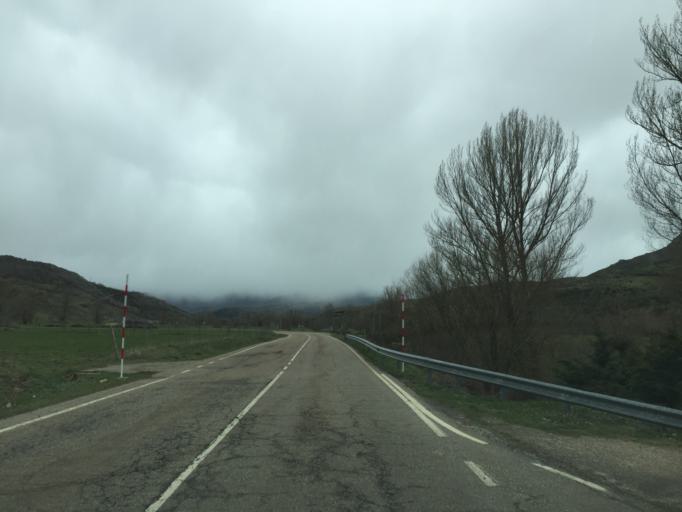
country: ES
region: Castille and Leon
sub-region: Provincia de Leon
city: San Emiliano
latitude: 42.9987
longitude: -5.9983
